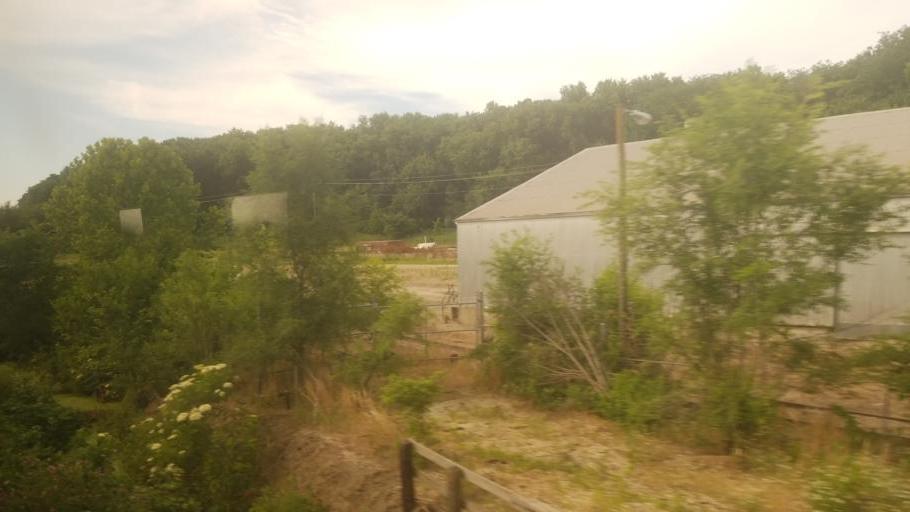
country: US
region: Kansas
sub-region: Douglas County
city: Lawrence
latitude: 38.9561
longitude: -95.1998
